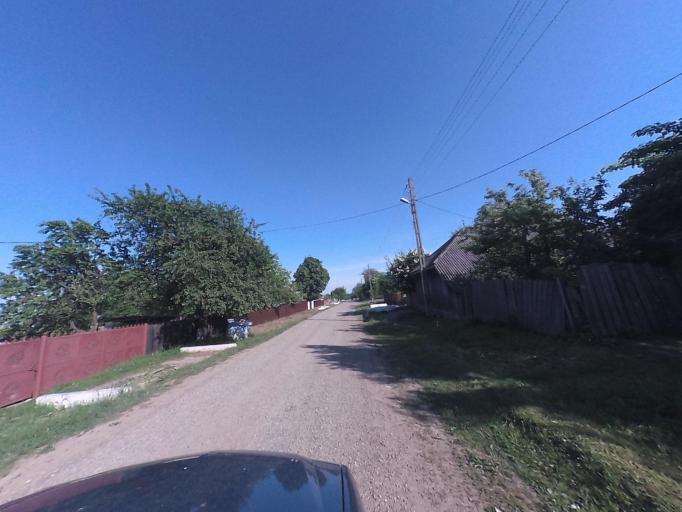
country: RO
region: Neamt
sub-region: Comuna Dulcesti
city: Dulcesti
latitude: 47.0041
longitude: 26.7724
